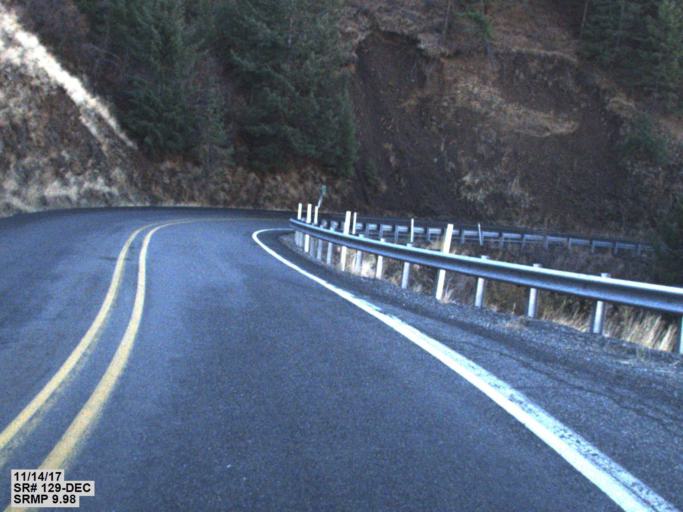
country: US
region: Washington
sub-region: Asotin County
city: Asotin
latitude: 46.0702
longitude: -117.2200
